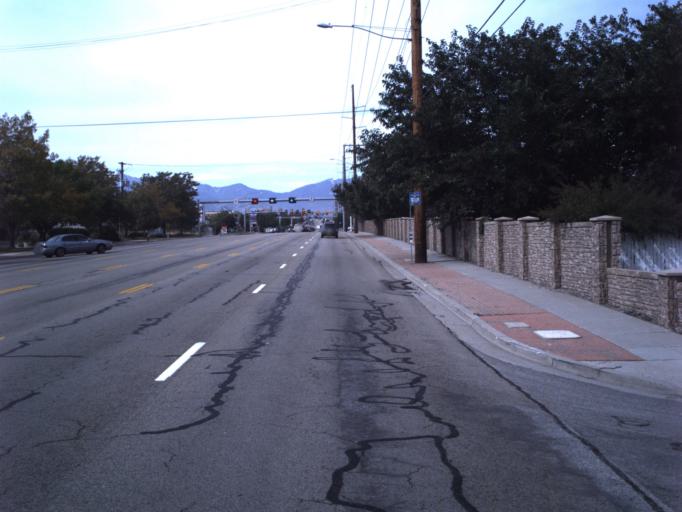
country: US
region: Utah
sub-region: Salt Lake County
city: Taylorsville
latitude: 40.6532
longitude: -111.9639
